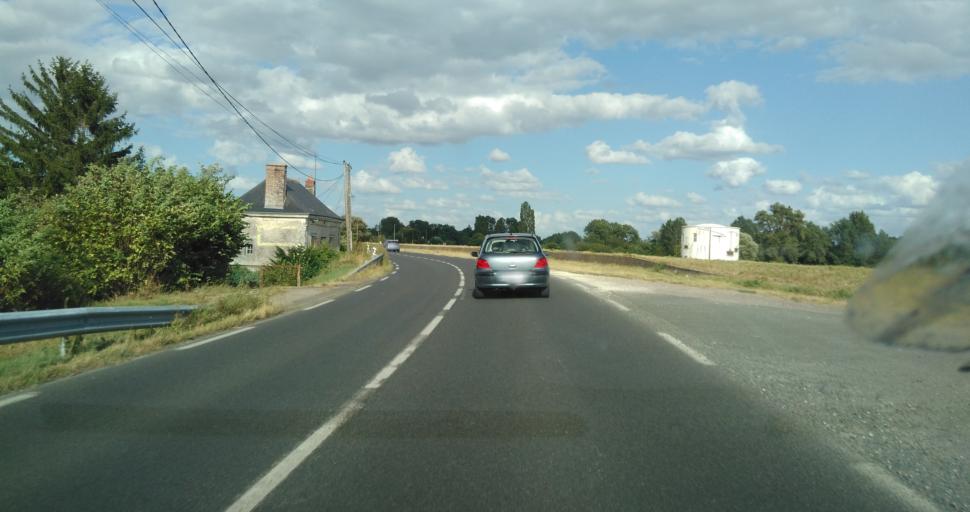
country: FR
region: Centre
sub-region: Departement d'Indre-et-Loire
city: Fondettes
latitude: 47.3830
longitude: 0.5825
